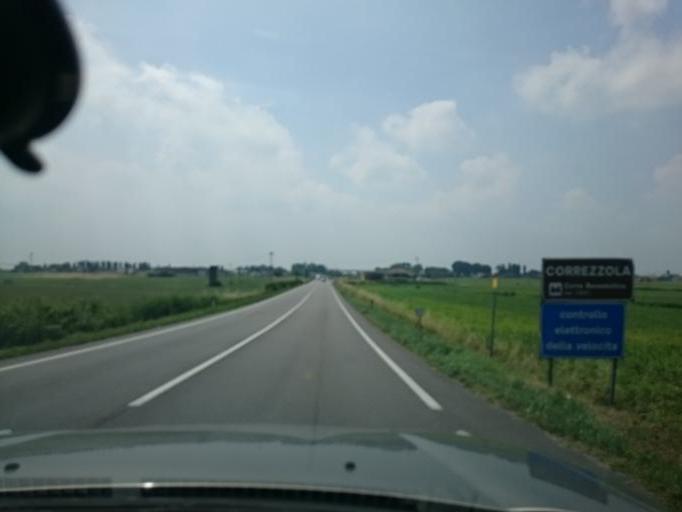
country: IT
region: Veneto
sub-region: Provincia di Padova
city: Codevigo
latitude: 45.2392
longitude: 12.1227
